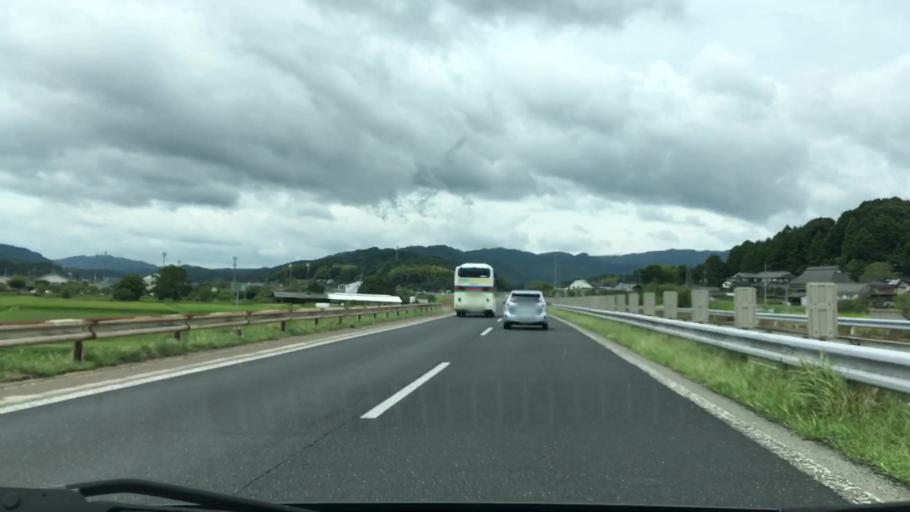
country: JP
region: Okayama
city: Tsuyama
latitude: 35.0607
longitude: 133.9050
